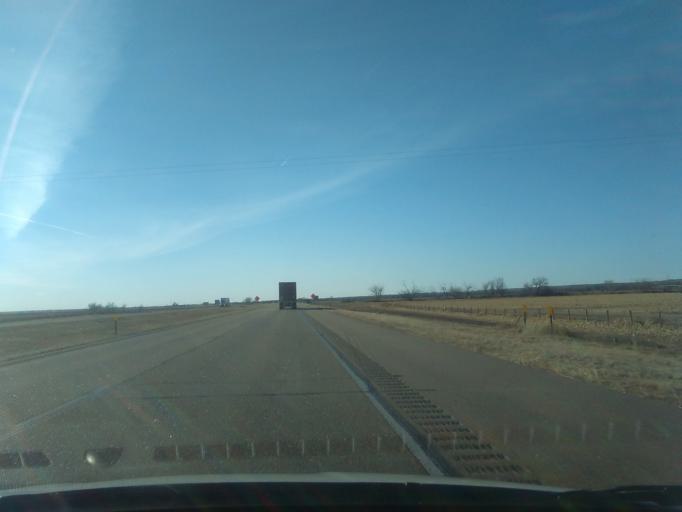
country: US
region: Colorado
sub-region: Sedgwick County
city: Julesburg
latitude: 41.0411
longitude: -102.1041
